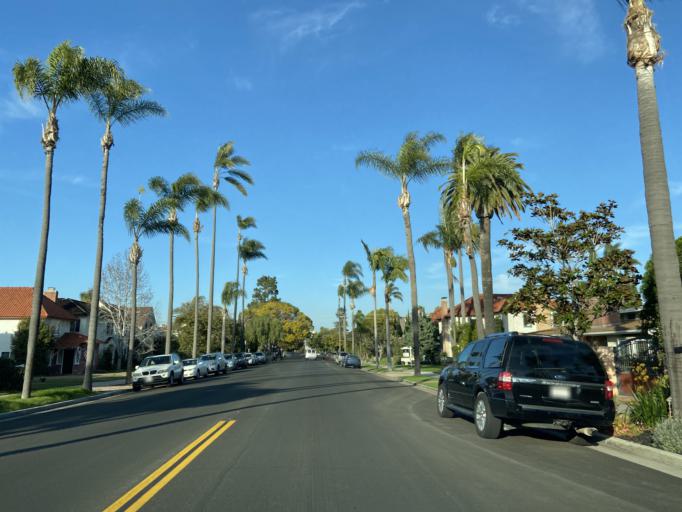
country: US
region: California
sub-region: San Diego County
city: Coronado
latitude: 32.6888
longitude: -117.1739
